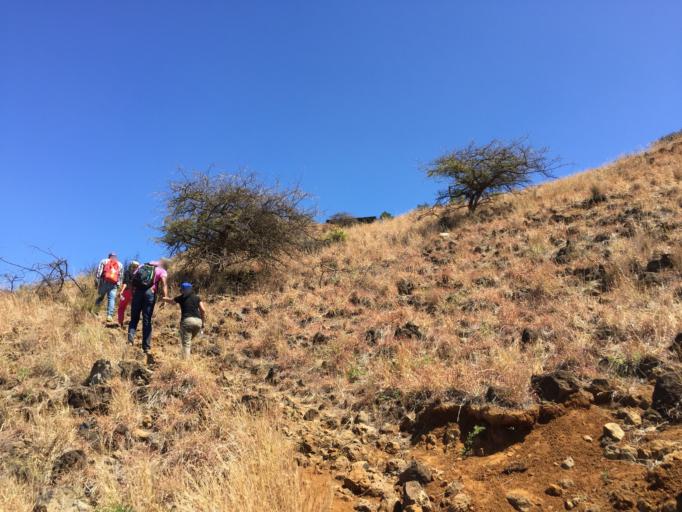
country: CV
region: Mosteiros
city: Porto dos Mosteiros
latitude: 15.0061
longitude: -24.3762
